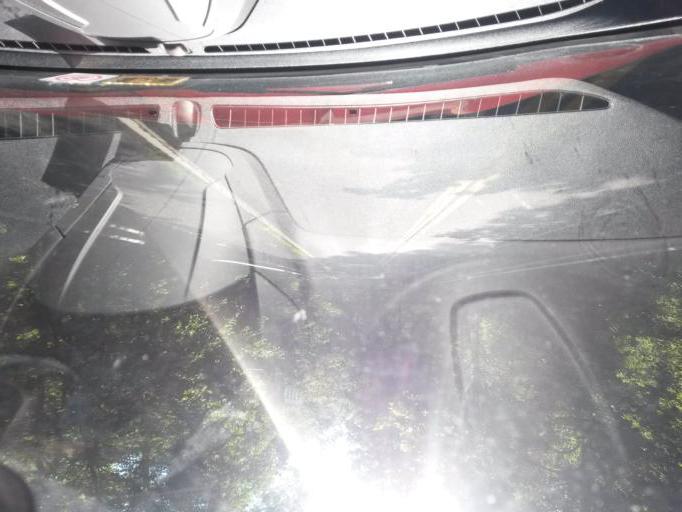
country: US
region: West Virginia
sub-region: Wyoming County
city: Pineville
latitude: 37.5161
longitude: -81.5826
